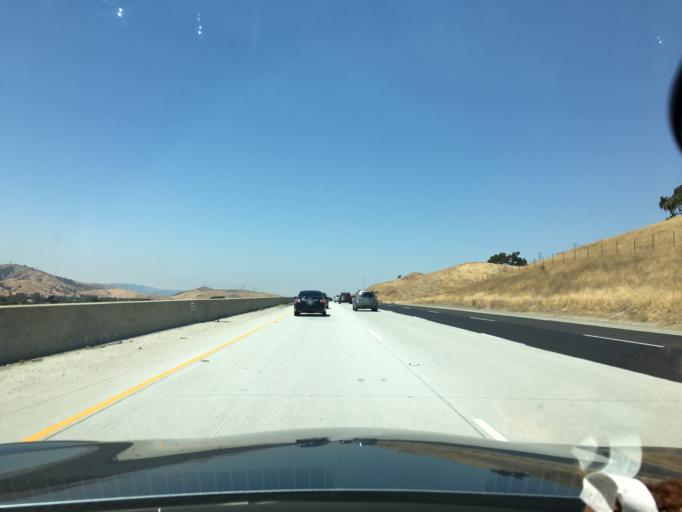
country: US
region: California
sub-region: Santa Clara County
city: Morgan Hill
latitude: 37.1998
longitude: -121.7062
